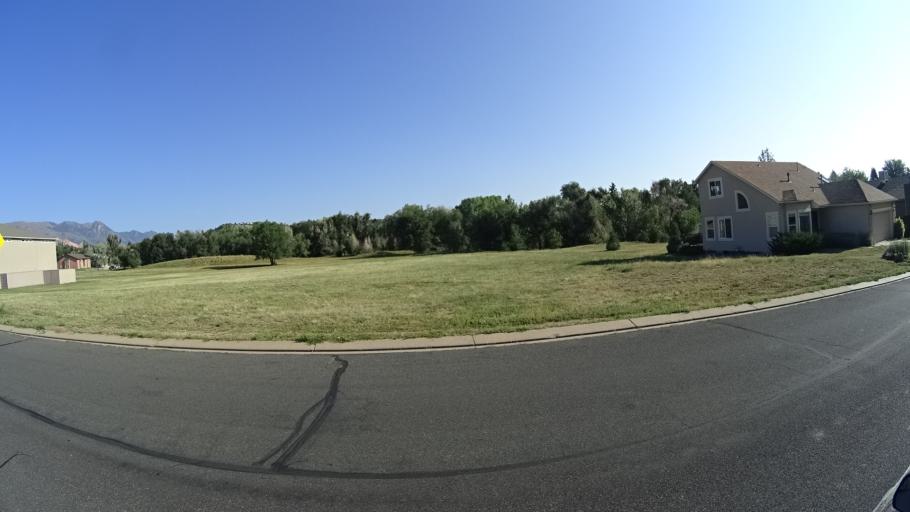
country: US
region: Colorado
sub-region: El Paso County
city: Colorado Springs
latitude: 38.8884
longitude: -104.8429
